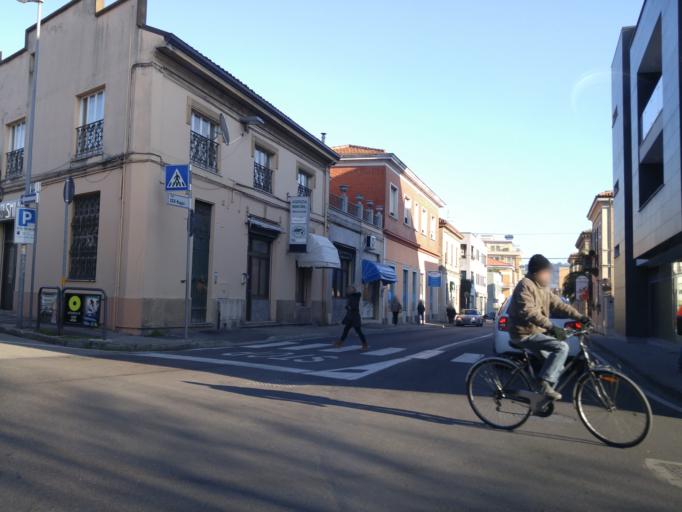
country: IT
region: The Marches
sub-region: Provincia di Pesaro e Urbino
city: Pesaro
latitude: 43.9058
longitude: 12.9075
